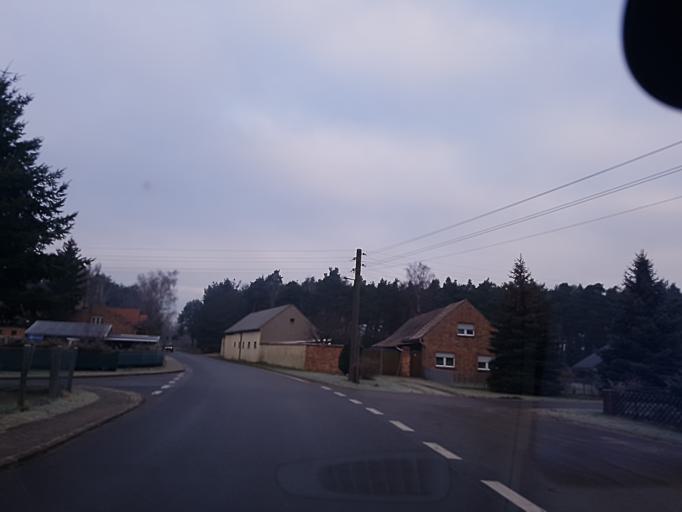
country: DE
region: Brandenburg
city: Finsterwalde
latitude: 51.6872
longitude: 13.7266
